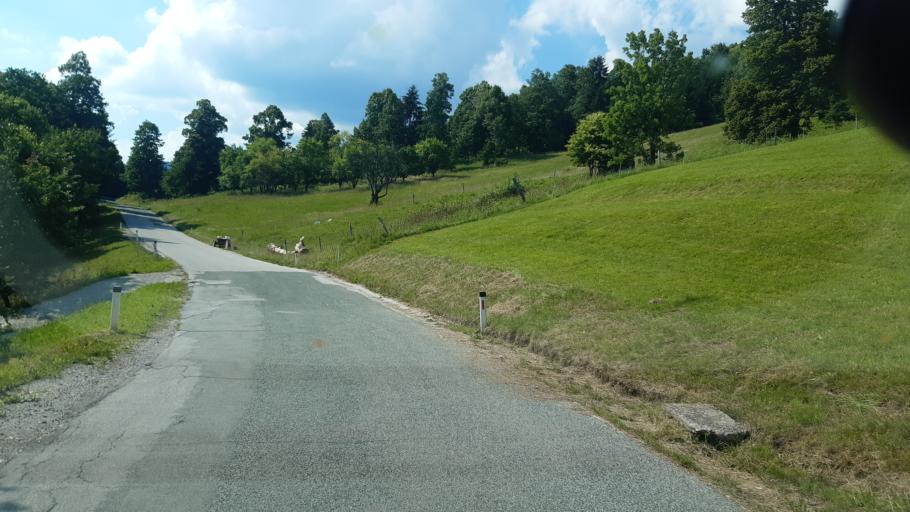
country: SI
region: Radovljica
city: Radovljica
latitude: 46.3693
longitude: 14.2223
